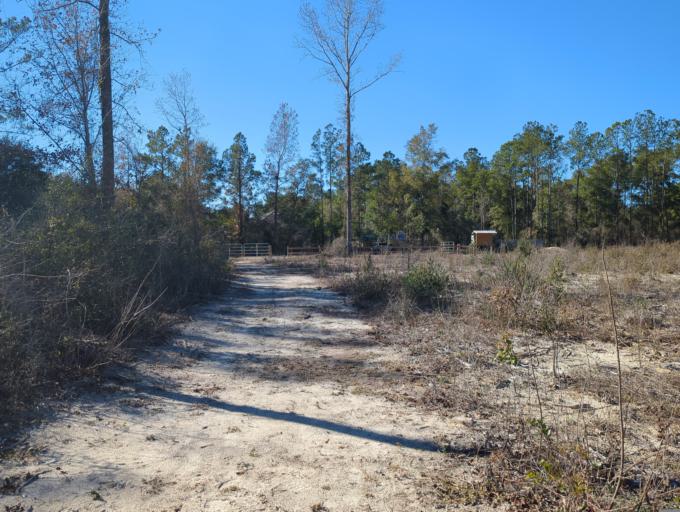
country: US
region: Florida
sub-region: Wakulla County
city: Crawfordville
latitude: 30.1828
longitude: -84.3338
